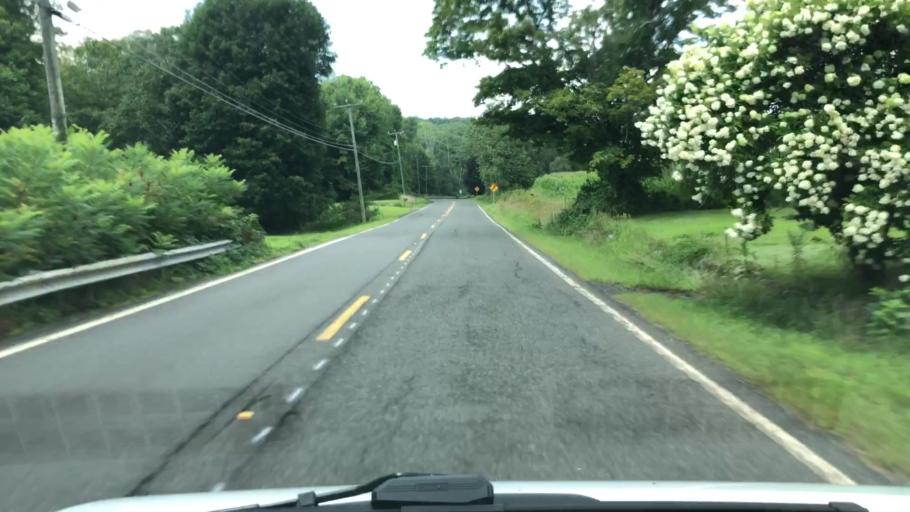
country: US
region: Massachusetts
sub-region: Franklin County
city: Conway
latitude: 42.5124
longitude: -72.7162
